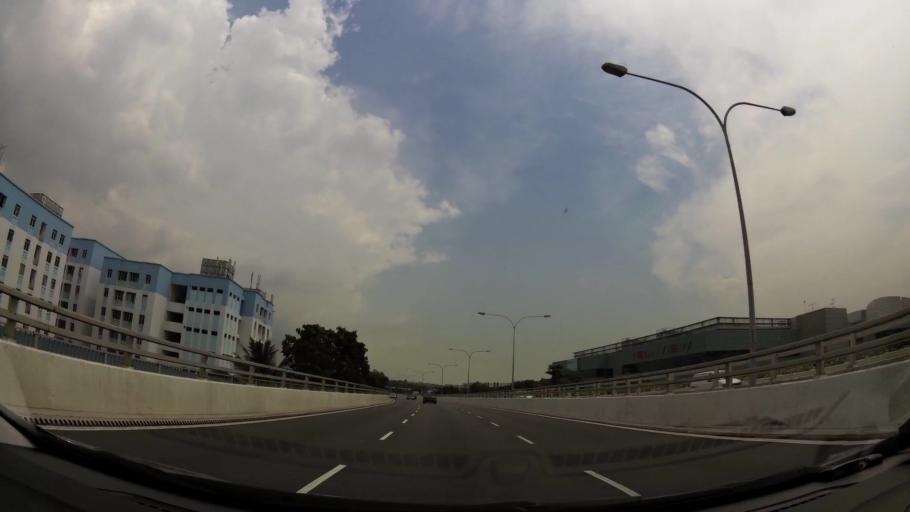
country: SG
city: Singapore
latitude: 1.3376
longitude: 103.9088
